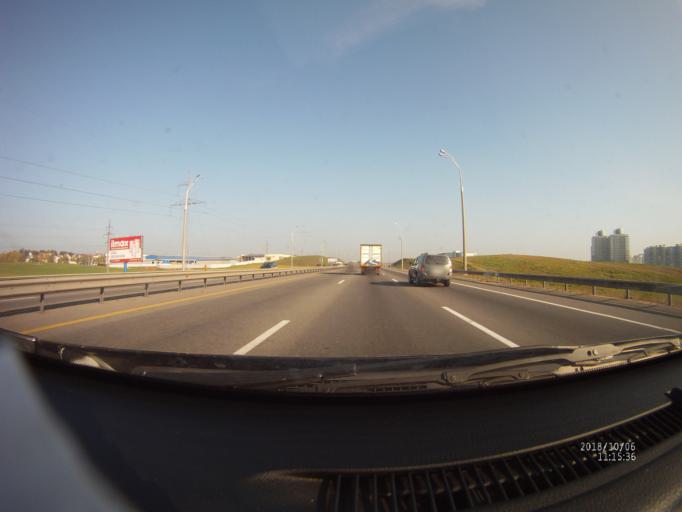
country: BY
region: Minsk
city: Zhdanovichy
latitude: 53.9314
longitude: 27.4221
